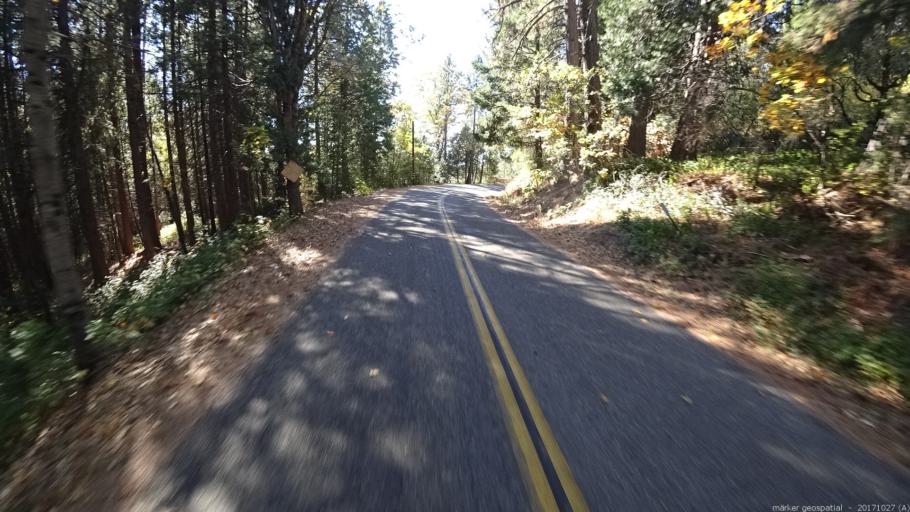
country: US
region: California
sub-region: Shasta County
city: Shingletown
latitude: 40.6898
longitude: -121.9148
